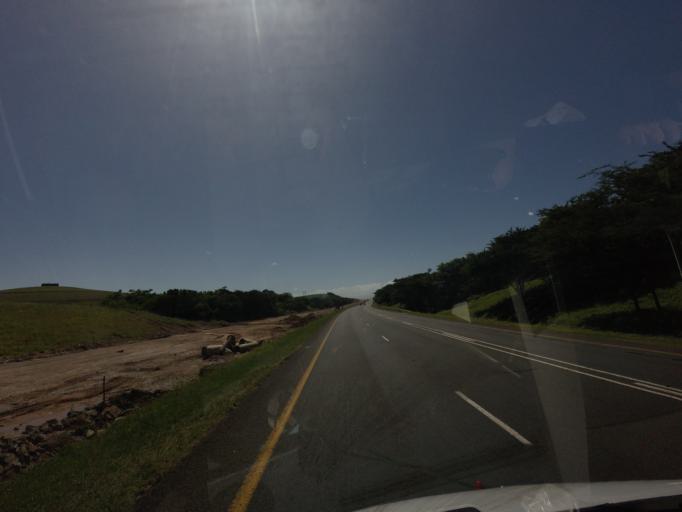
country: ZA
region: KwaZulu-Natal
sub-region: uThungulu District Municipality
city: eSikhawini
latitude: -28.9306
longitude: 31.7648
